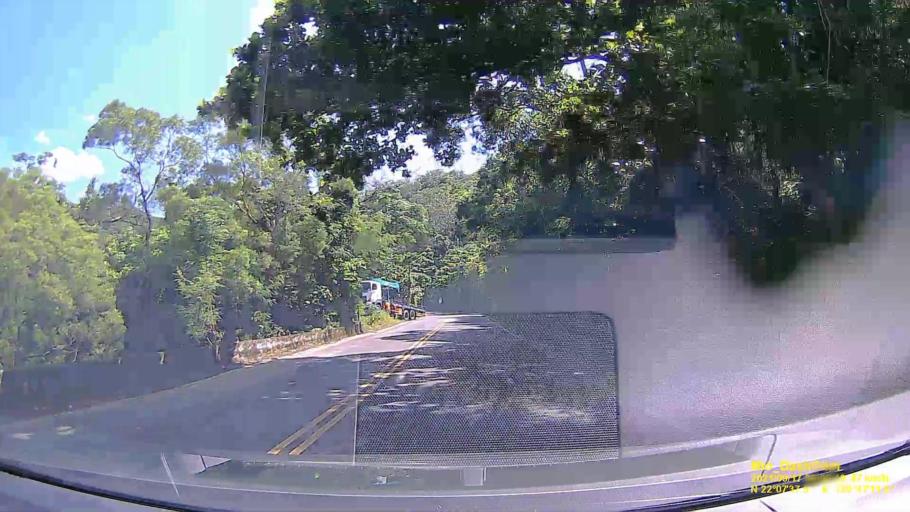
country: TW
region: Taiwan
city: Hengchun
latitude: 22.1271
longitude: 120.7866
